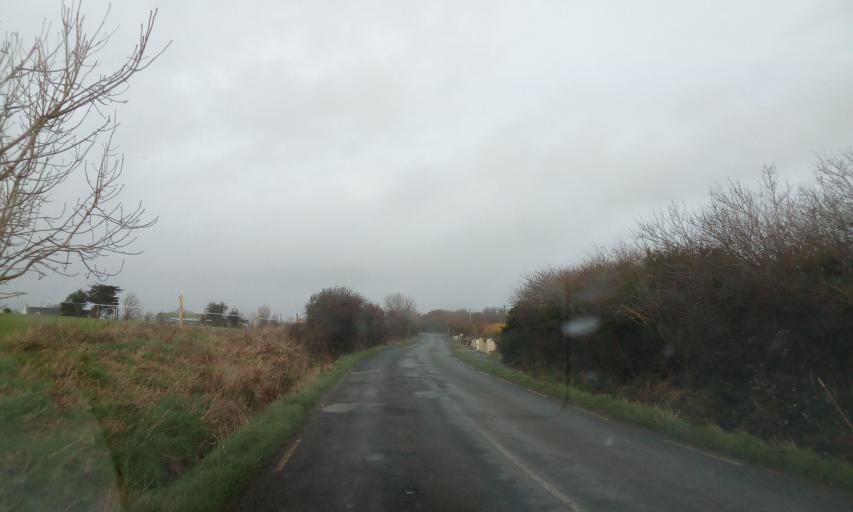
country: IE
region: Leinster
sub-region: Loch Garman
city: New Ross
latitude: 52.2571
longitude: -6.7551
